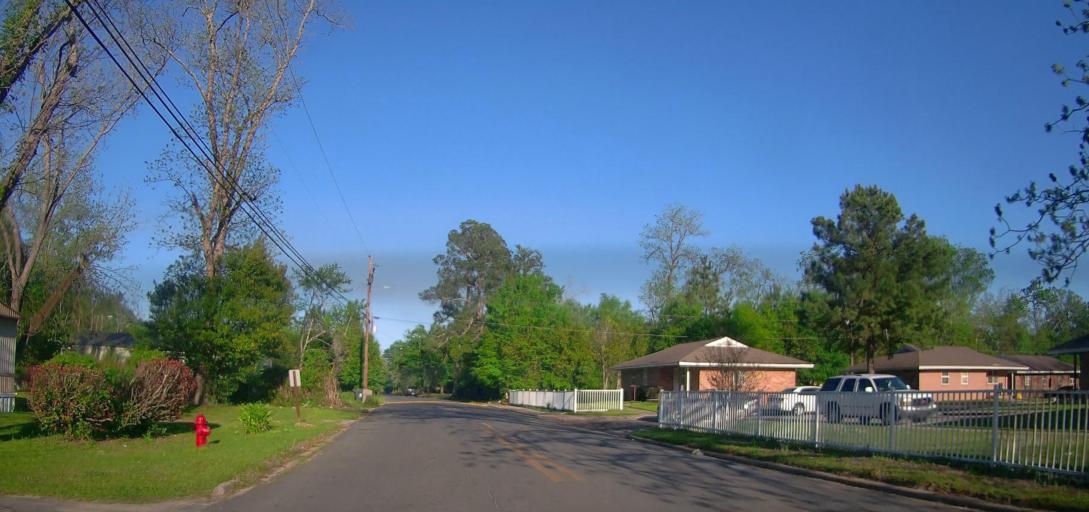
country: US
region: Georgia
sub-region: Macon County
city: Oglethorpe
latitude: 32.2907
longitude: -84.0704
